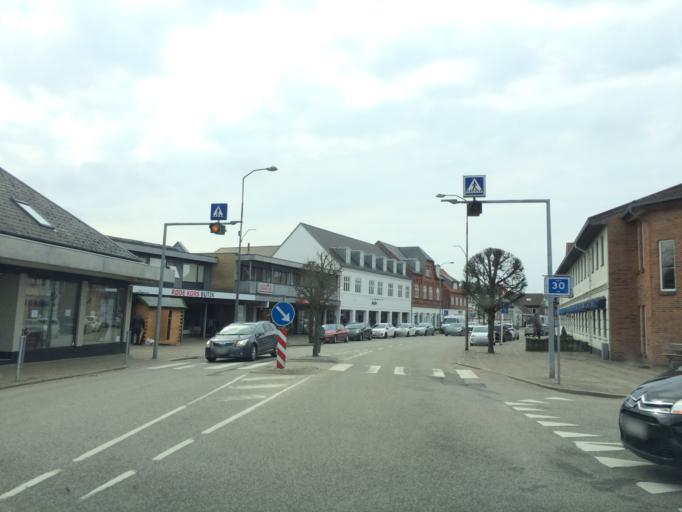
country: DK
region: Central Jutland
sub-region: Ringkobing-Skjern Kommune
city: Tarm
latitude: 55.9088
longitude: 8.5216
